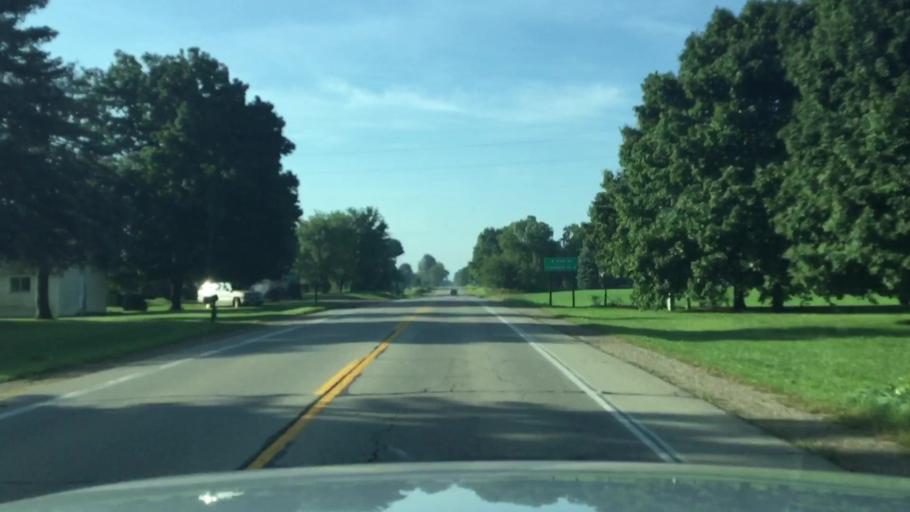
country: US
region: Michigan
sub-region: Lenawee County
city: Manitou Beach-Devils Lake
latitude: 41.9447
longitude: -84.3672
